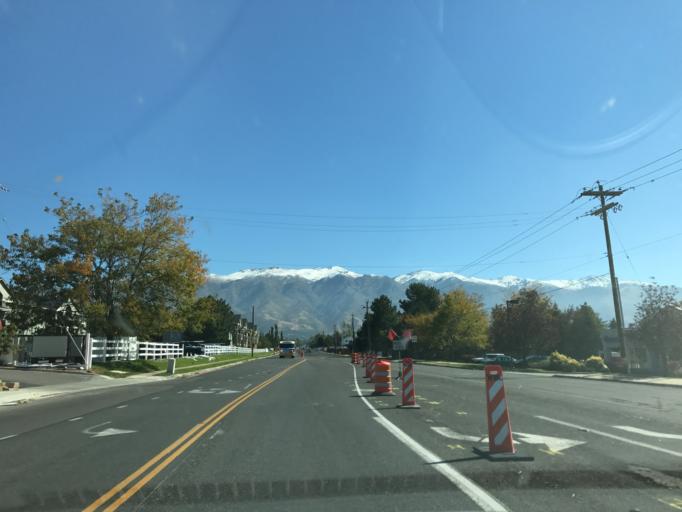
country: US
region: Utah
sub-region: Davis County
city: Hill Air Force Bace
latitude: 41.0893
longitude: -111.9730
